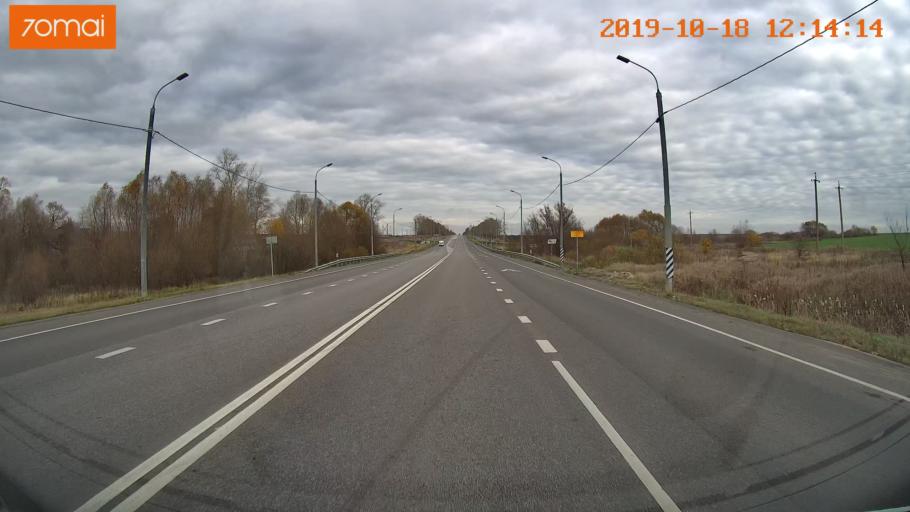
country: RU
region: Rjazan
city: Zakharovo
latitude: 54.4282
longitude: 39.3798
